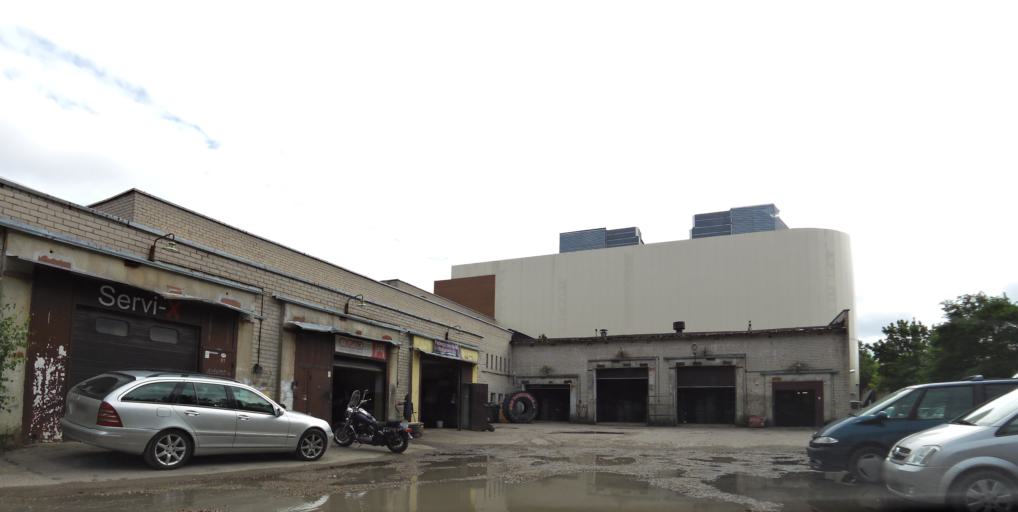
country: LT
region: Vilnius County
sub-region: Vilnius
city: Vilnius
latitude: 54.7117
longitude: 25.2754
